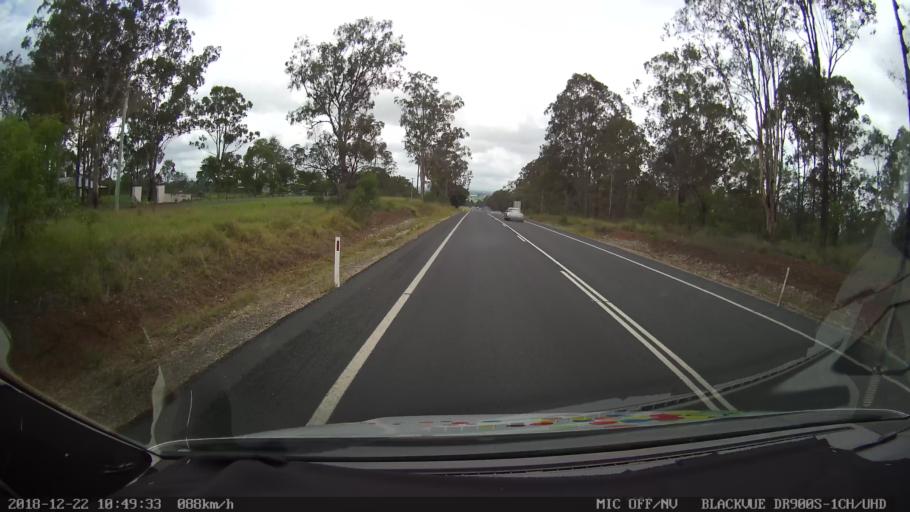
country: AU
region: New South Wales
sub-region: Clarence Valley
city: South Grafton
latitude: -29.6842
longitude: 152.8694
